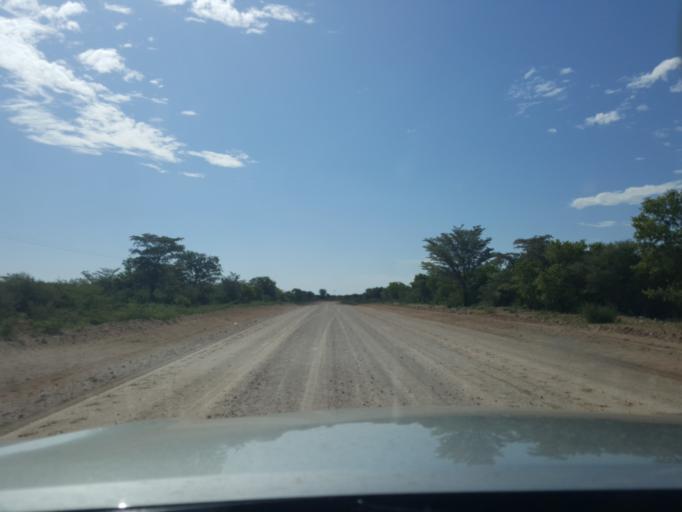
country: BW
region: Kweneng
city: Khudumelapye
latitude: -23.7805
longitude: 24.7739
